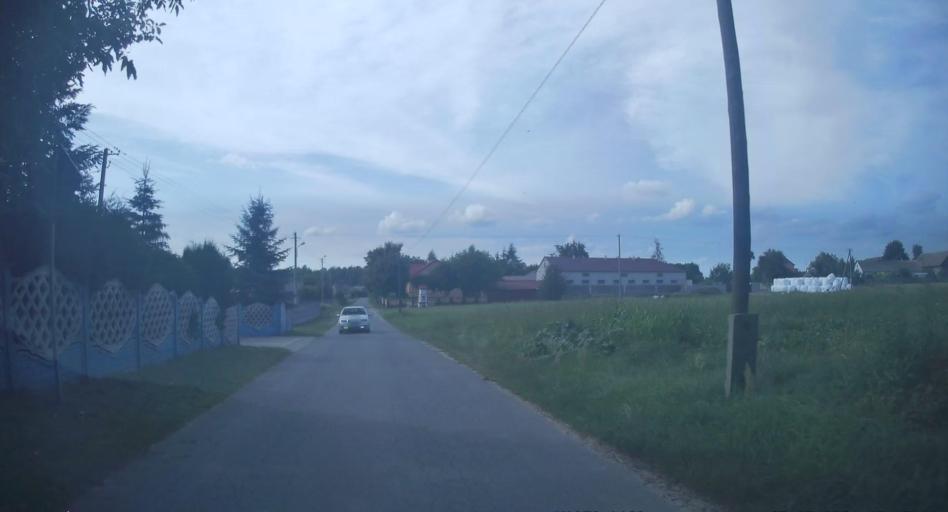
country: PL
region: Lodz Voivodeship
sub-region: Powiat rawski
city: Rawa Mazowiecka
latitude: 51.6929
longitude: 20.2544
